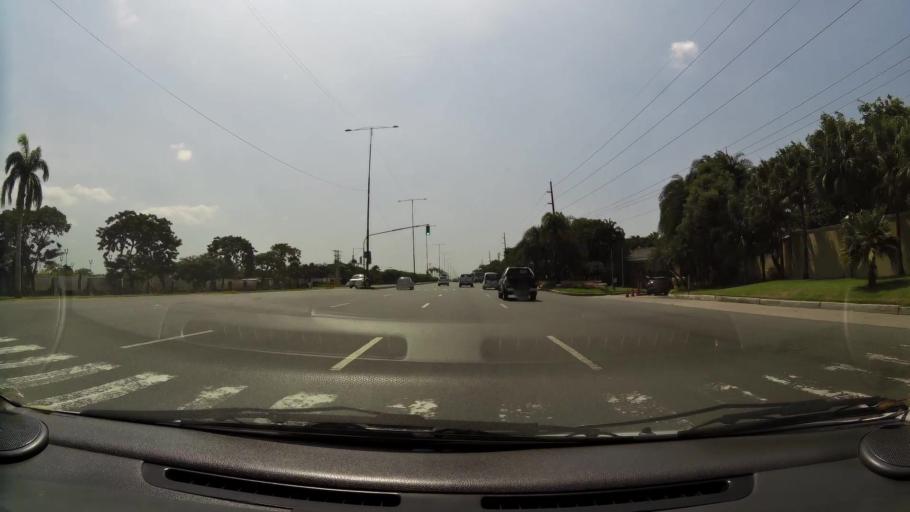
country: EC
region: Guayas
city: Eloy Alfaro
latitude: -2.0968
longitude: -79.8738
